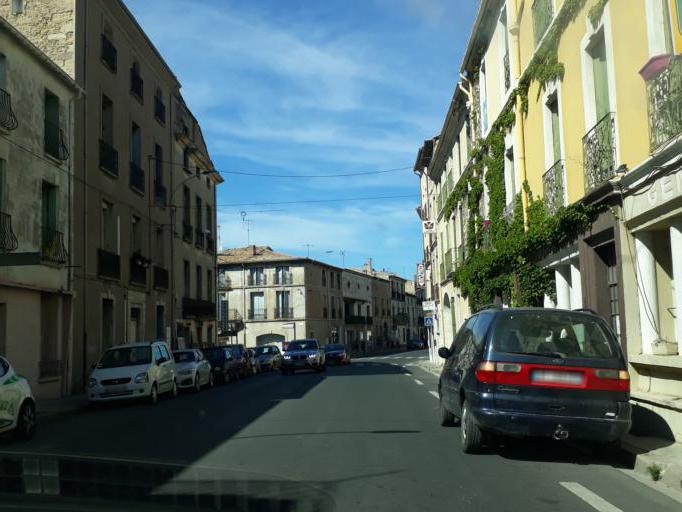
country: FR
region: Languedoc-Roussillon
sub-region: Departement de l'Herault
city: Pezenas
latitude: 43.4580
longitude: 3.4259
